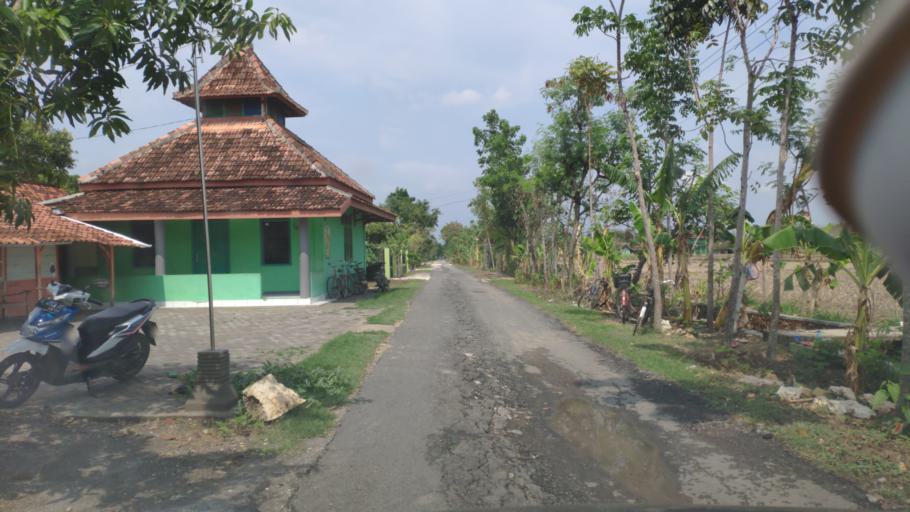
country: ID
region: Central Java
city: Balongrejo
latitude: -7.0055
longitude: 111.3786
